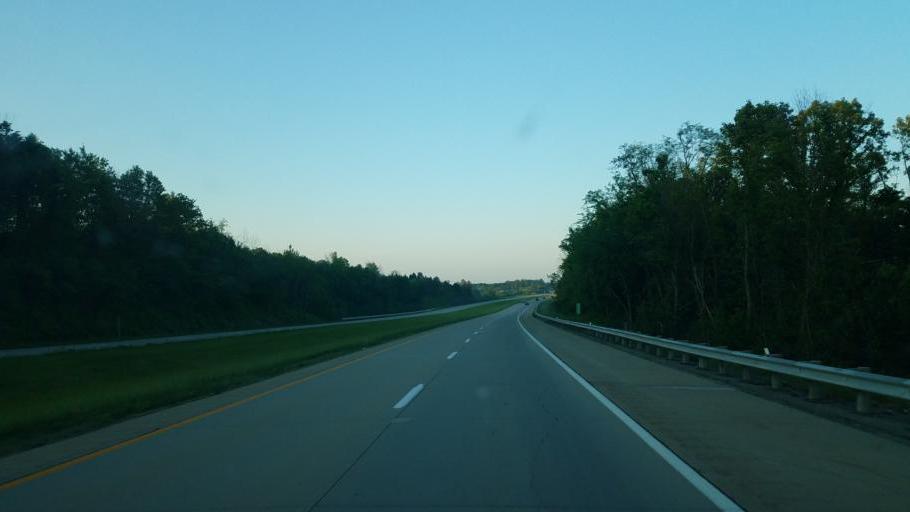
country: US
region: Ohio
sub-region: Washington County
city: Devola
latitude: 39.5539
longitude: -81.4484
